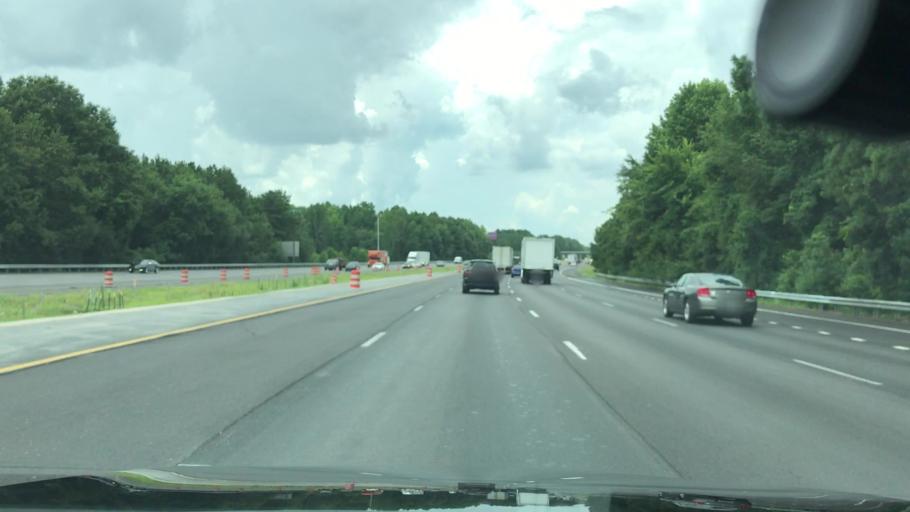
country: US
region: South Carolina
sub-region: Richland County
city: Dentsville
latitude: 34.1064
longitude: -80.9616
